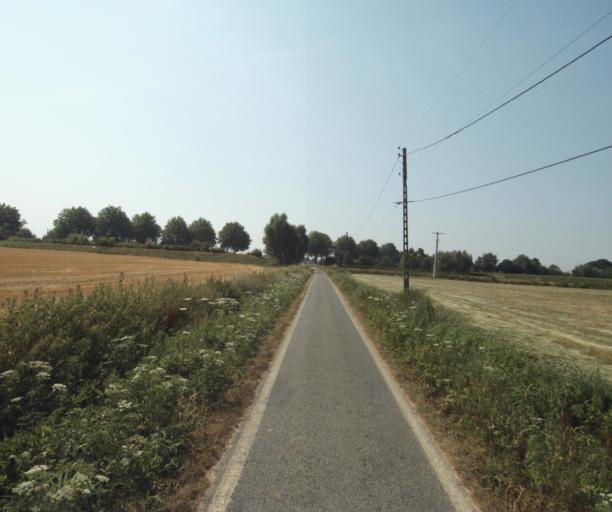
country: FR
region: Nord-Pas-de-Calais
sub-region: Departement du Nord
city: Quesnoy-sur-Deule
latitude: 50.7195
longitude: 3.0142
